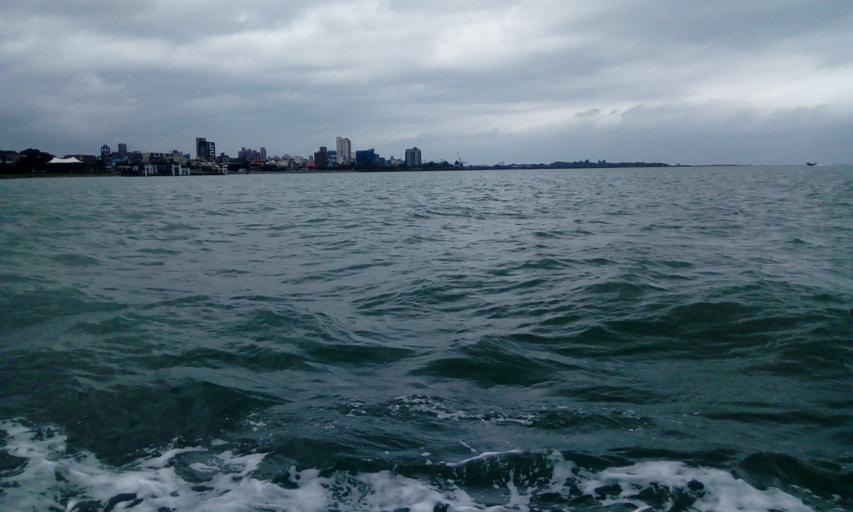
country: TW
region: Taipei
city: Taipei
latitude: 25.1629
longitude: 121.4364
